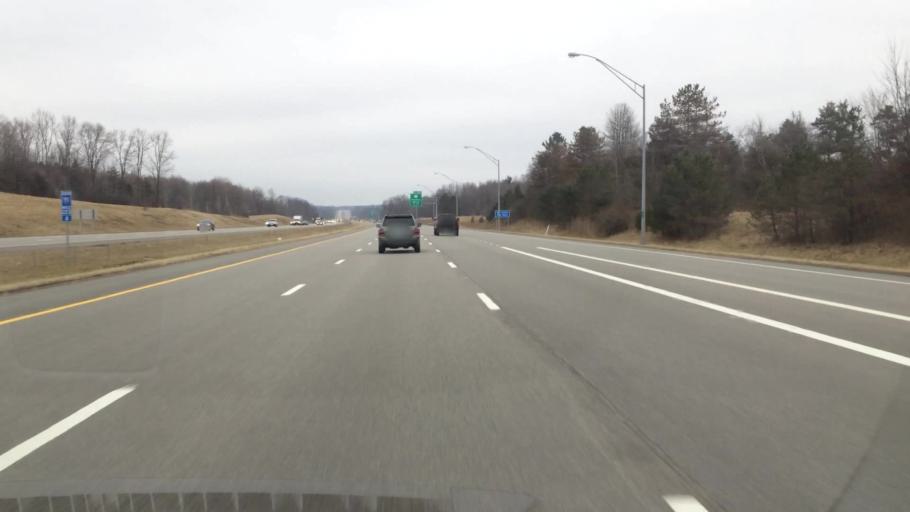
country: US
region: Ohio
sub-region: Medina County
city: Brunswick
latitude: 41.2065
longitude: -81.7935
